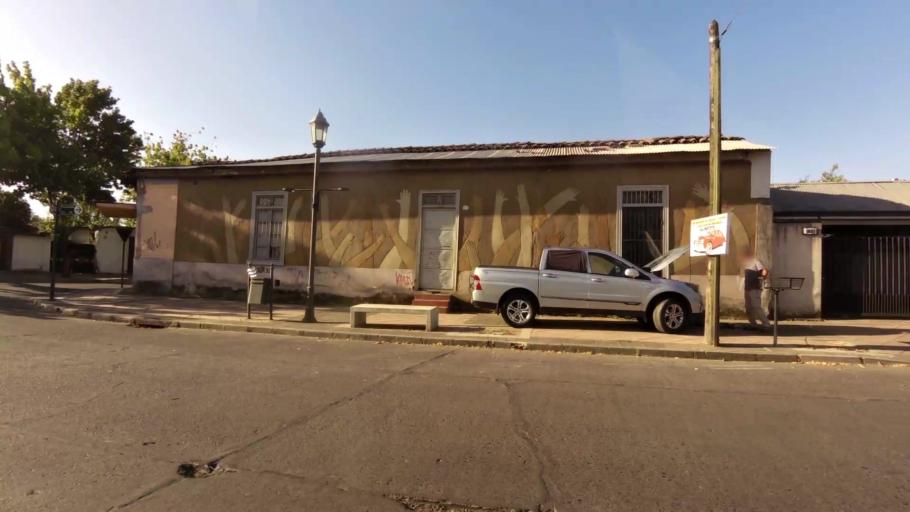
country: CL
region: Maule
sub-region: Provincia de Talca
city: Talca
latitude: -35.4341
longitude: -71.6575
